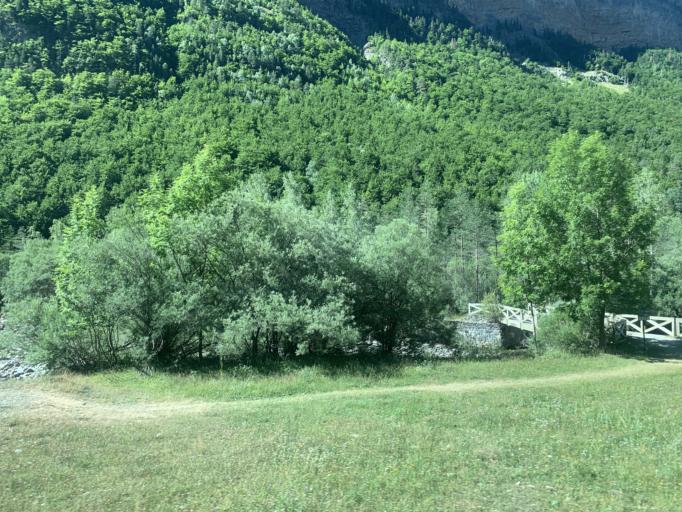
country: ES
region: Aragon
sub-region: Provincia de Huesca
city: Broto
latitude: 42.6497
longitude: -0.0646
